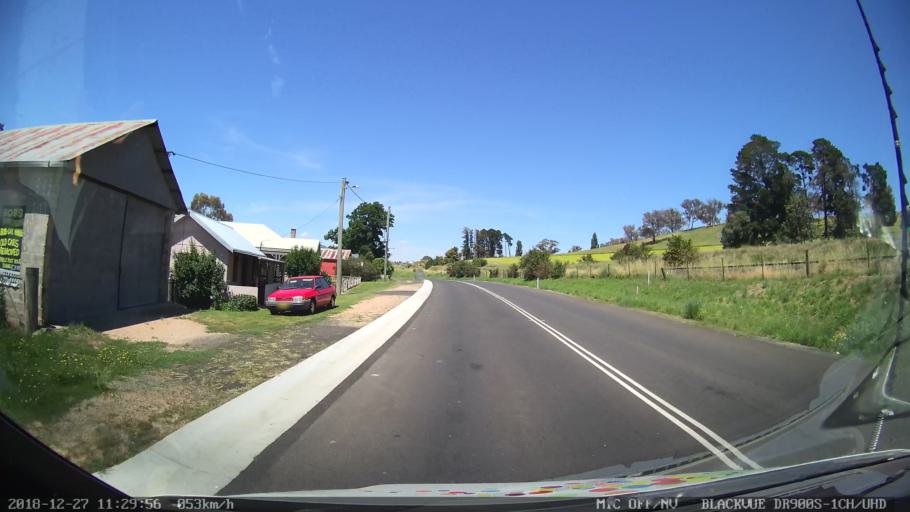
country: AU
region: New South Wales
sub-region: Bathurst Regional
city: Perthville
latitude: -33.4842
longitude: 149.5485
